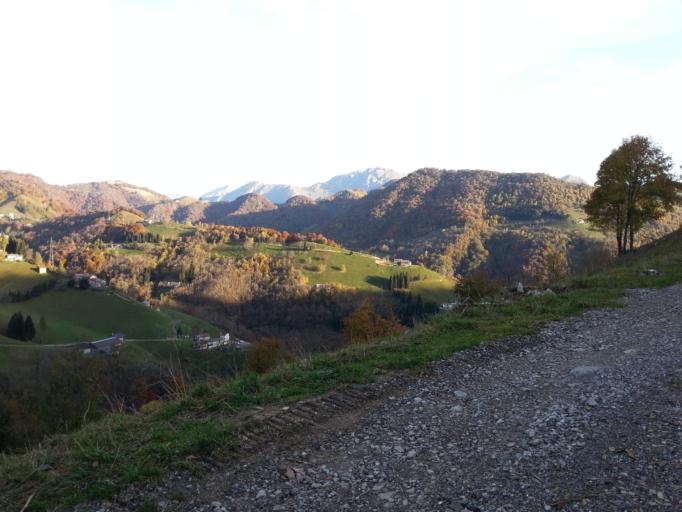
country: IT
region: Lombardy
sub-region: Provincia di Lecco
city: Morterone
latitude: 45.8751
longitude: 9.4893
